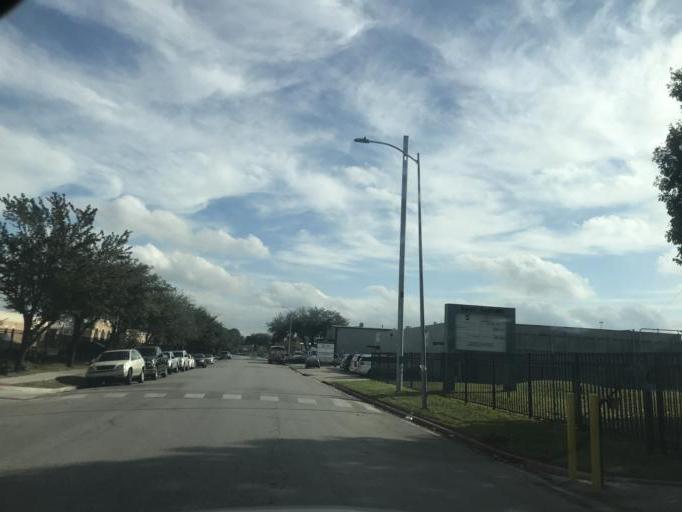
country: US
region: Texas
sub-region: Harris County
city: Piney Point Village
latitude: 29.7282
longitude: -95.4949
